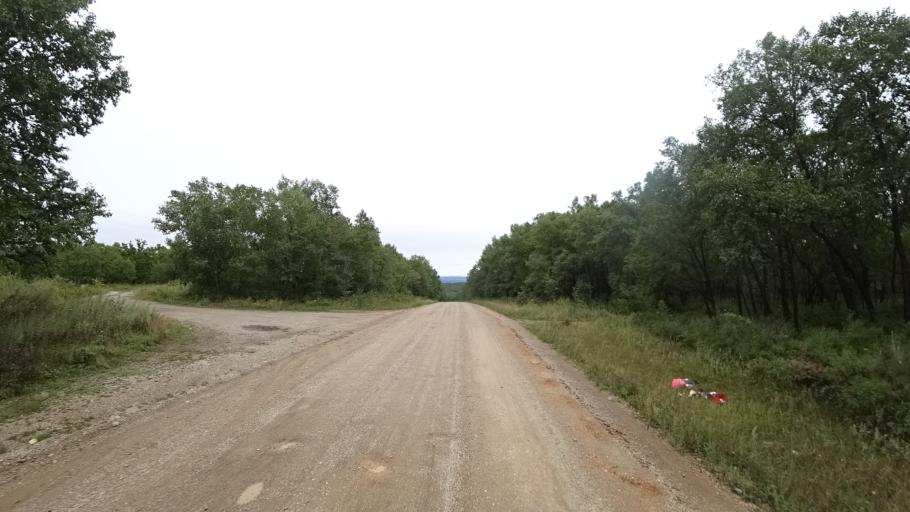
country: RU
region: Primorskiy
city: Ivanovka
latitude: 44.0353
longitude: 132.5016
